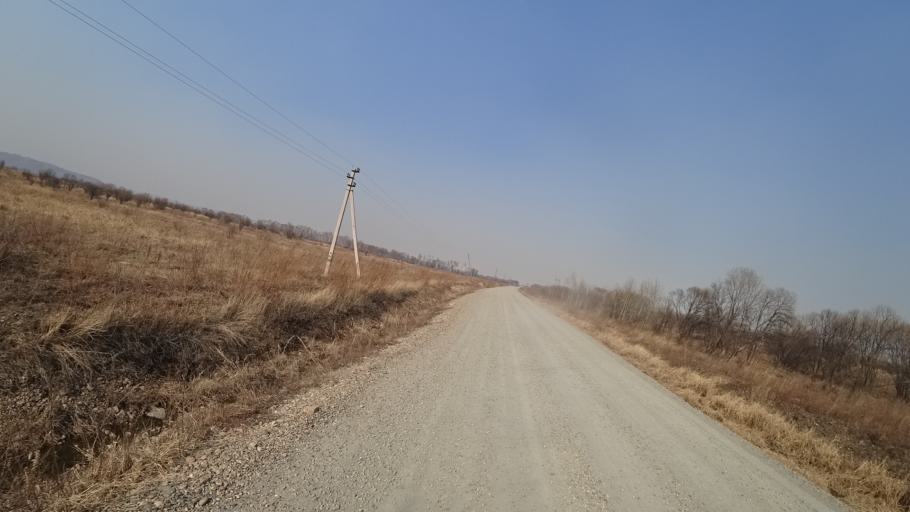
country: RU
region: Amur
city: Novobureyskiy
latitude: 49.8099
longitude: 129.9684
